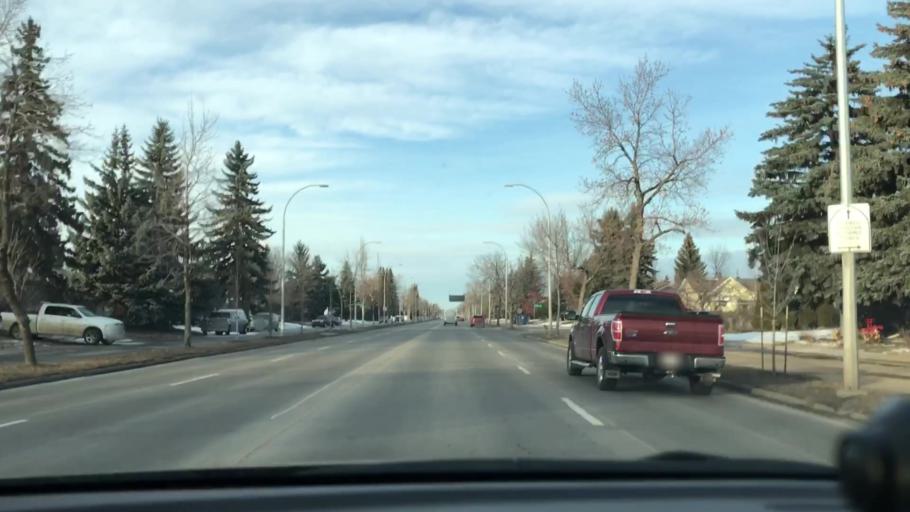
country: CA
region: Alberta
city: Edmonton
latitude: 53.5271
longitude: -113.4429
